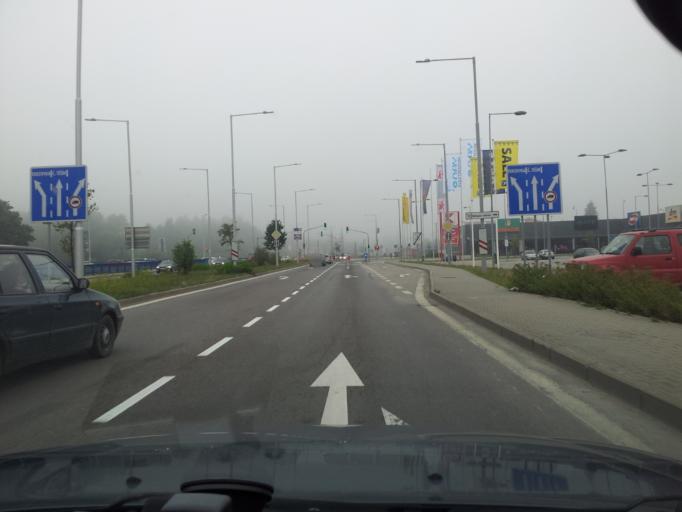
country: SK
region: Zilinsky
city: Cadca
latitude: 49.4417
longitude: 18.7884
